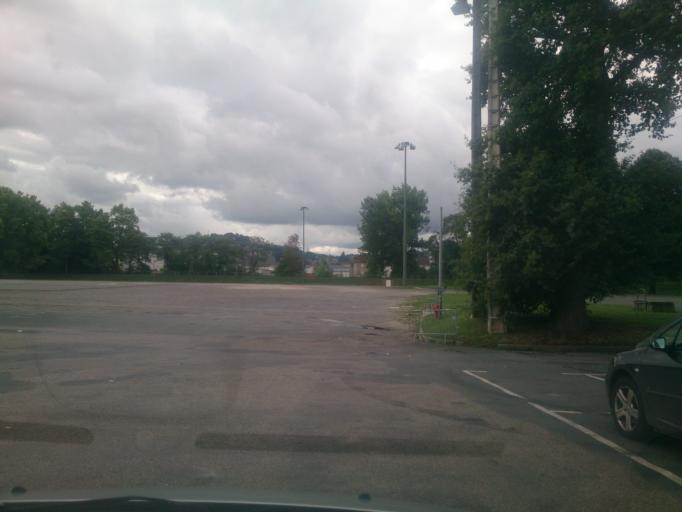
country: FR
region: Limousin
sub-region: Departement de la Correze
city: Brive-la-Gaillarde
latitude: 45.1649
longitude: 1.5433
